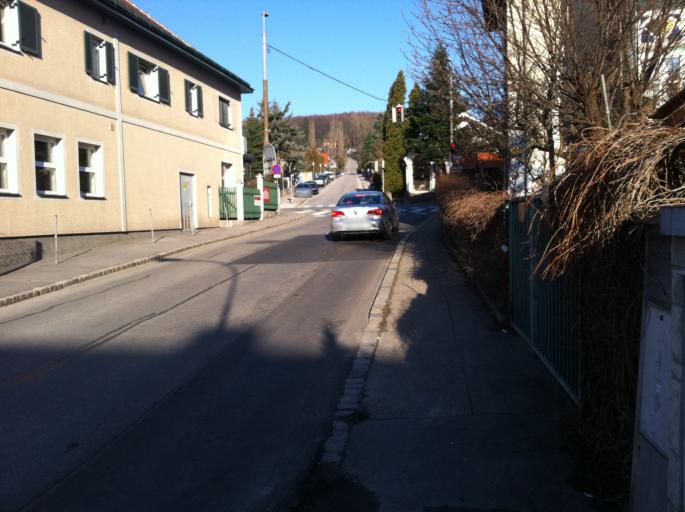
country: AT
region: Lower Austria
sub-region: Politischer Bezirk Wien-Umgebung
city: Gablitz
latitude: 48.2308
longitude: 16.1483
